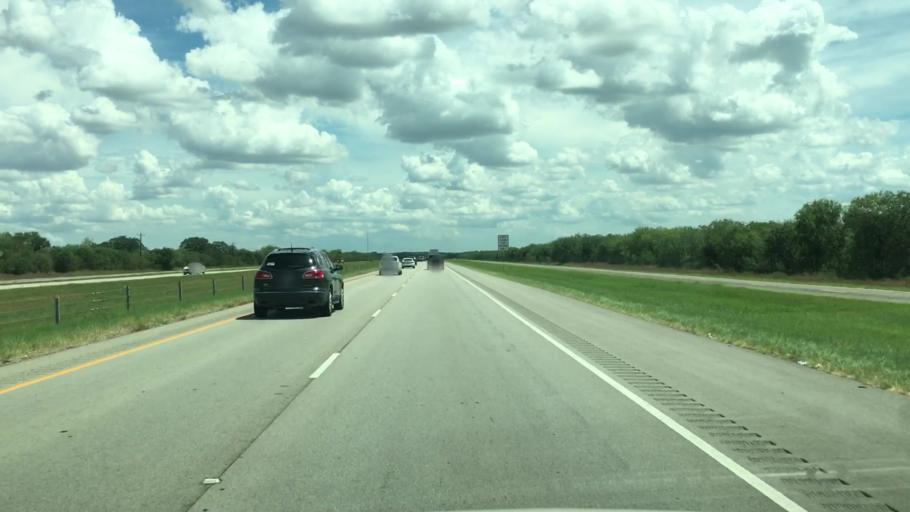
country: US
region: Texas
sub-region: Live Oak County
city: George West
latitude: 28.2806
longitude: -97.9560
